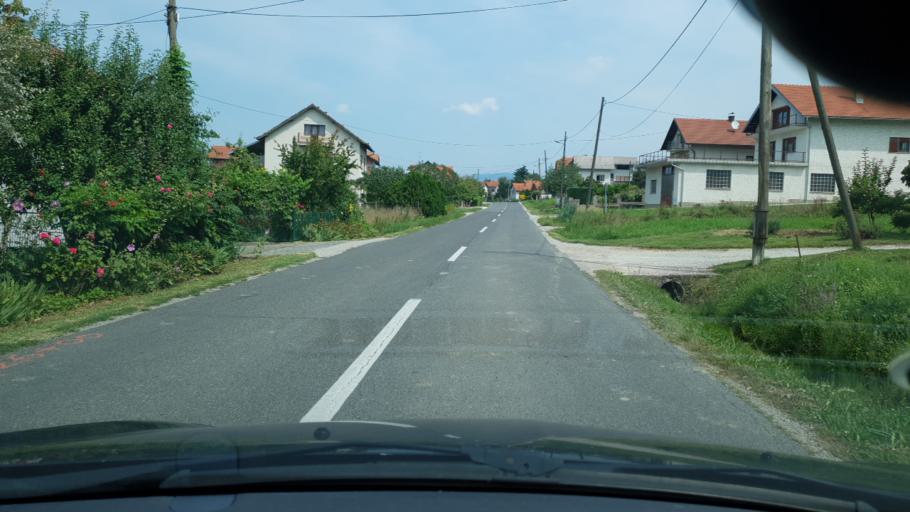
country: HR
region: Krapinsko-Zagorska
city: Marija Bistrica
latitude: 46.0164
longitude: 16.1060
